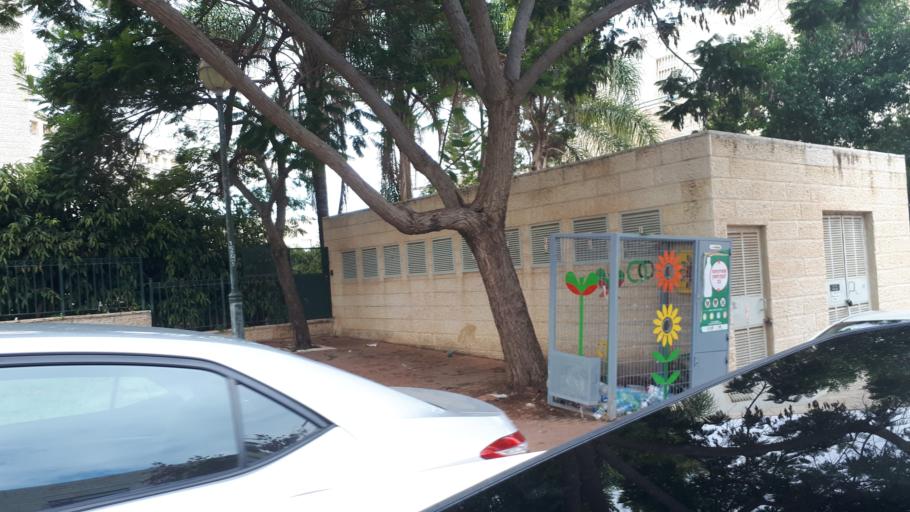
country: IL
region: Central District
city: Modiin
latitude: 31.9057
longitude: 35.0100
